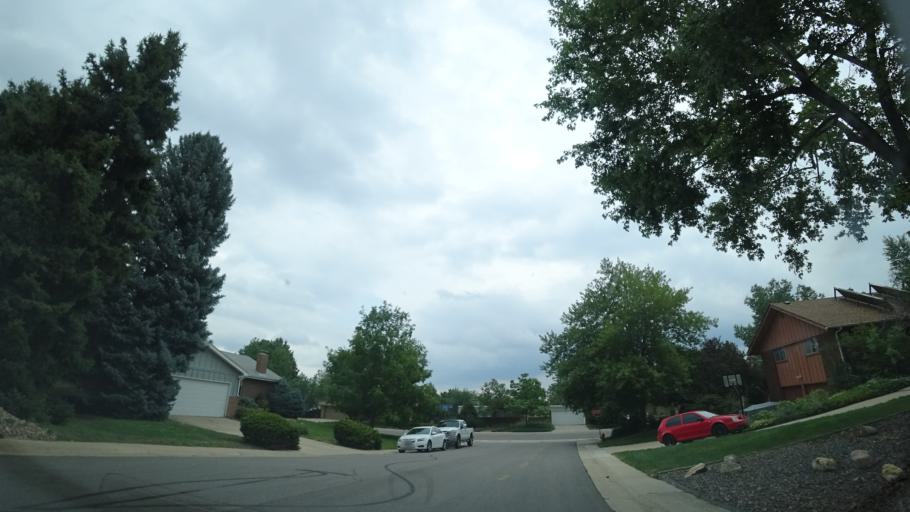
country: US
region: Colorado
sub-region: Jefferson County
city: West Pleasant View
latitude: 39.6999
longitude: -105.1503
